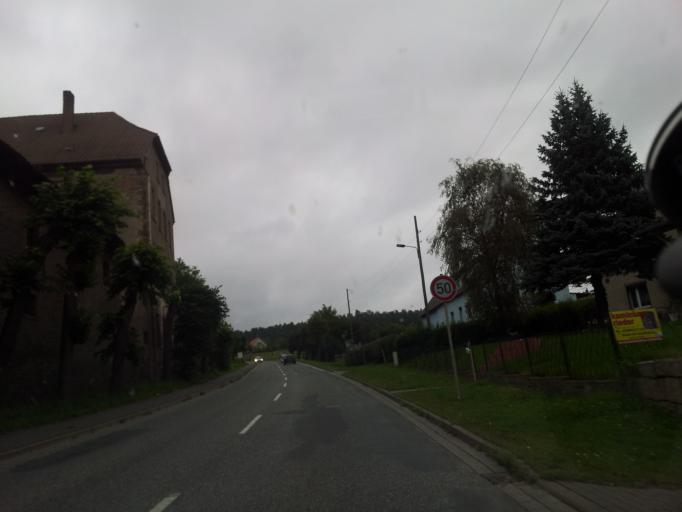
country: DE
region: Saxony-Anhalt
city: Blankenburg
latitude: 51.7785
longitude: 10.9684
